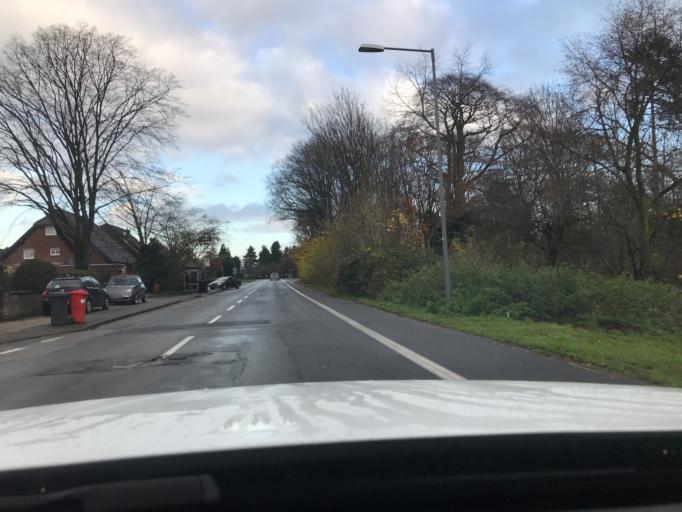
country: DE
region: North Rhine-Westphalia
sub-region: Regierungsbezirk Dusseldorf
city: Krefeld
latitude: 51.3846
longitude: 6.6003
